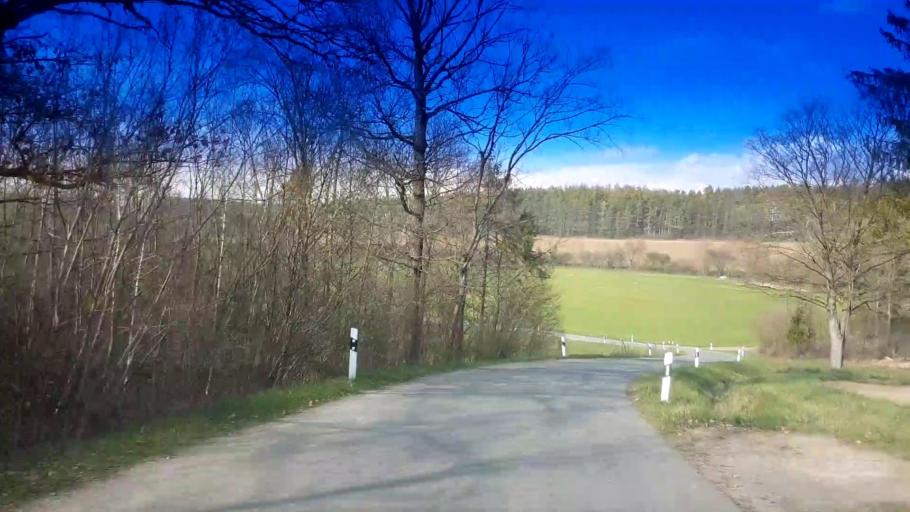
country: DE
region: Bavaria
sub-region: Upper Franconia
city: Harsdorf
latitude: 50.0316
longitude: 11.5881
